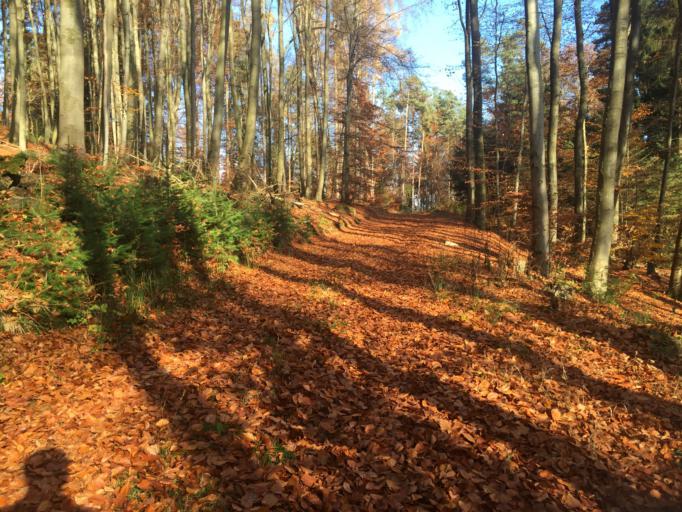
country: DE
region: Rheinland-Pfalz
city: Carlsberg
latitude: 49.4724
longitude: 8.0591
